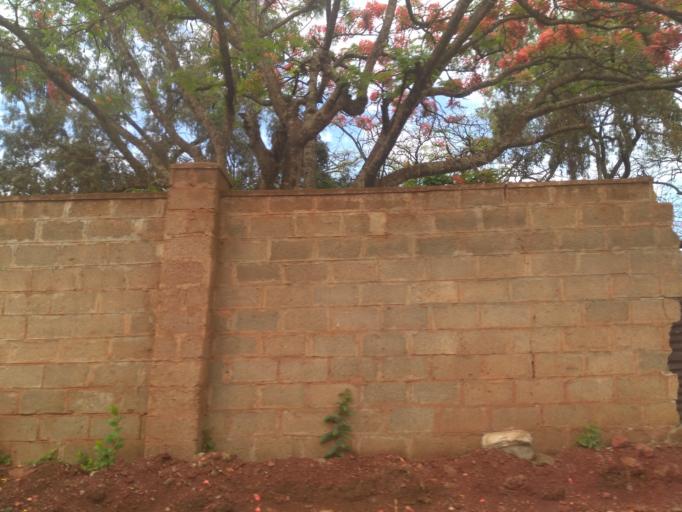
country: UG
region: Eastern Region
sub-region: Jinja District
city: Jinja
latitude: 0.4375
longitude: 33.1844
